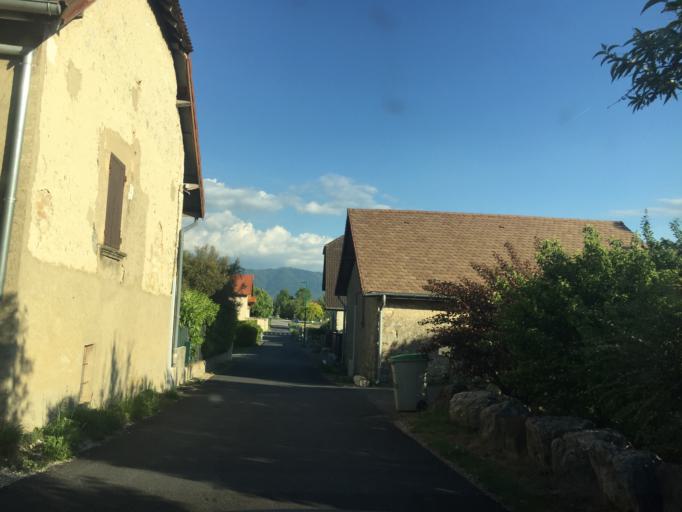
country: FR
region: Rhone-Alpes
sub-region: Departement de la Savoie
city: Les Marches
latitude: 45.4969
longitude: 5.9894
